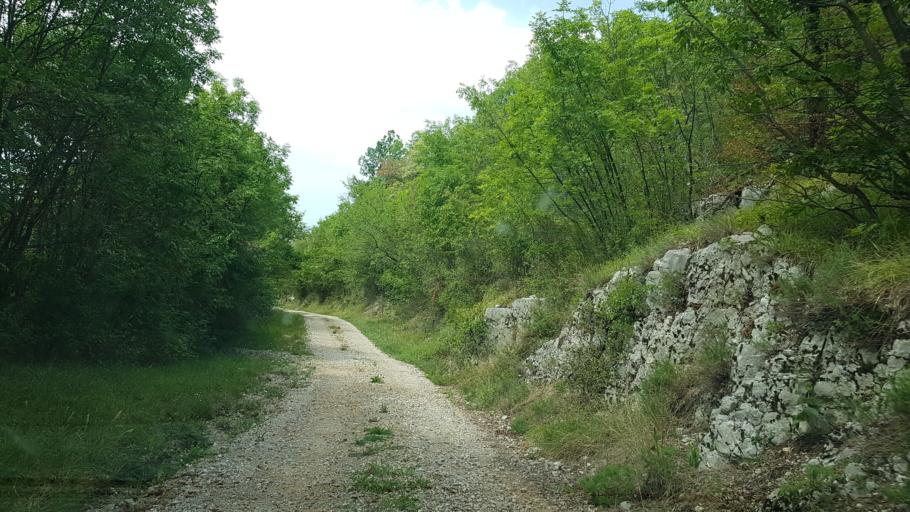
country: SI
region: Nova Gorica
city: Solkan
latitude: 46.0086
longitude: 13.6433
